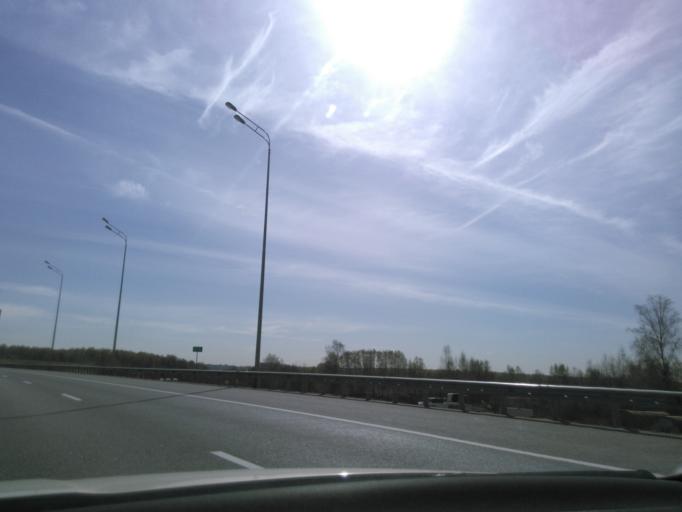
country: RU
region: Moskovskaya
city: Novopodrezkovo
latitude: 55.9537
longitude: 37.3810
